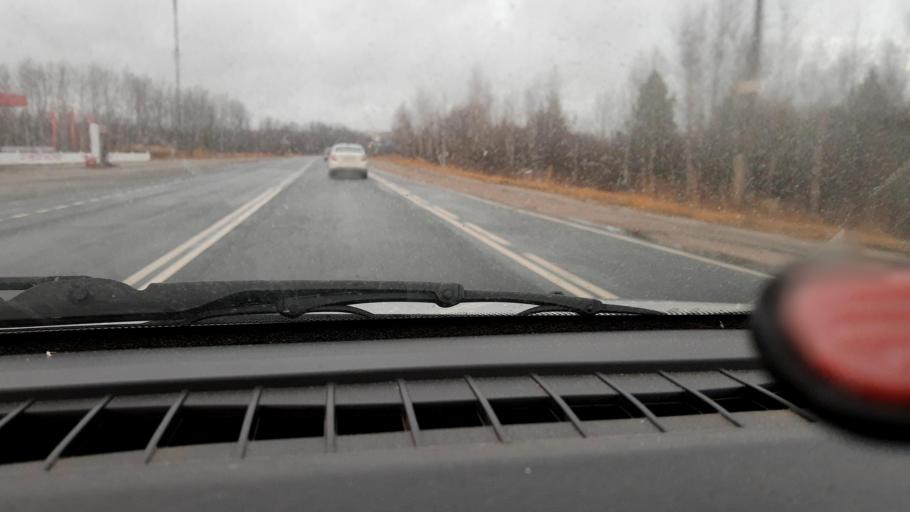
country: RU
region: Nizjnij Novgorod
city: Krasnyye Baki
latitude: 57.0861
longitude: 45.1476
